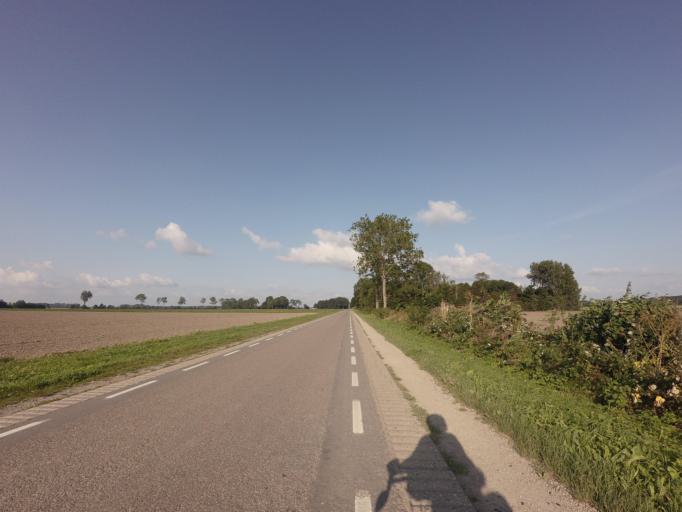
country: NL
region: Flevoland
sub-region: Gemeente Noordoostpolder
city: Ens
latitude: 52.6822
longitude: 5.8296
